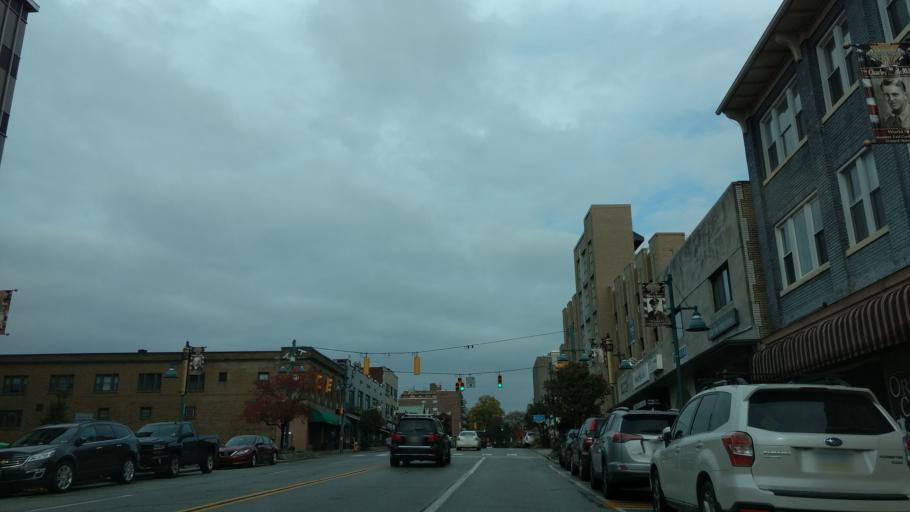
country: US
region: Pennsylvania
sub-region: Allegheny County
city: Dormont
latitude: 40.3810
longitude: -80.0443
